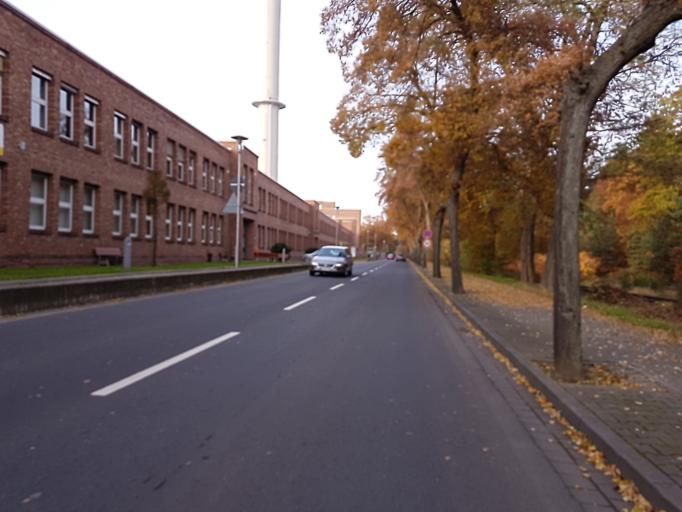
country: DE
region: Bavaria
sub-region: Regierungsbezirk Unterfranken
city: Elsenfeld
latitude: 49.8296
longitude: 9.1522
